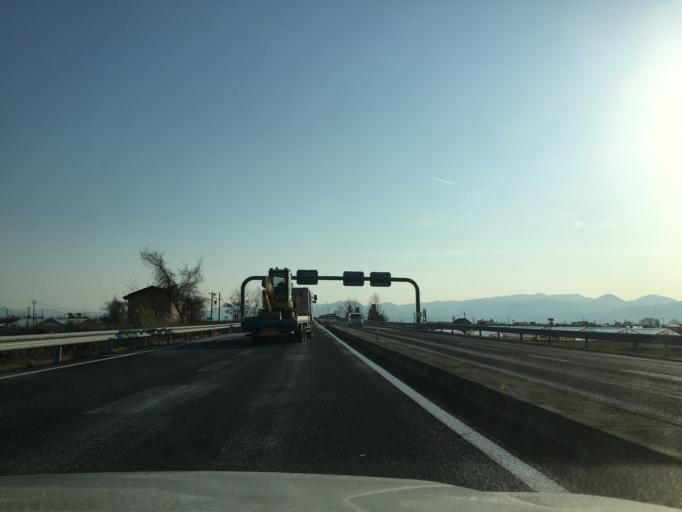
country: JP
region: Yamagata
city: Tendo
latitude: 38.3114
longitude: 140.3131
